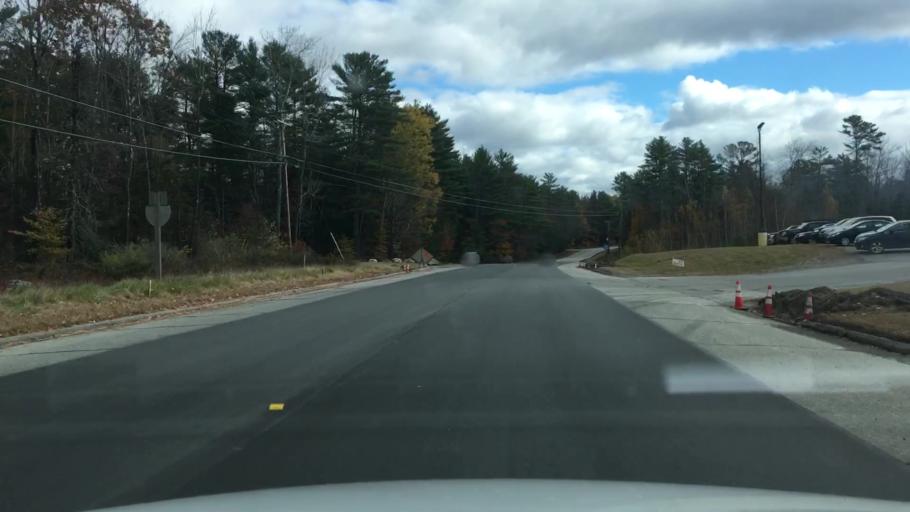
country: US
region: Maine
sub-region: Sagadahoc County
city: Richmond
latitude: 44.0991
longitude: -69.8650
